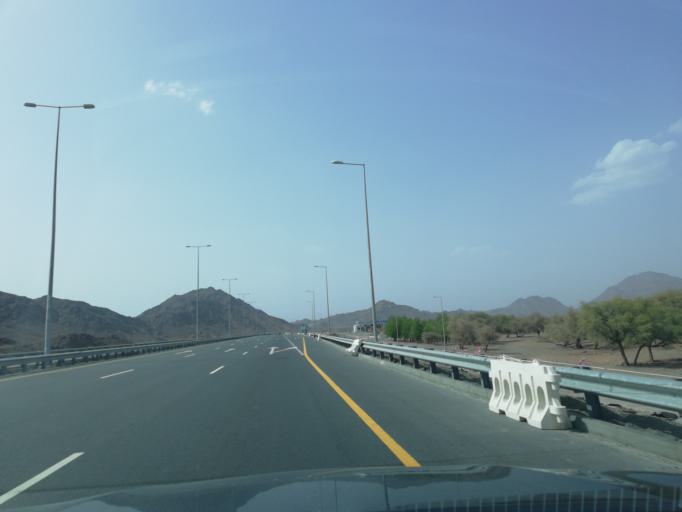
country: OM
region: Ash Sharqiyah
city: Ibra'
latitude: 22.9447
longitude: 58.2481
